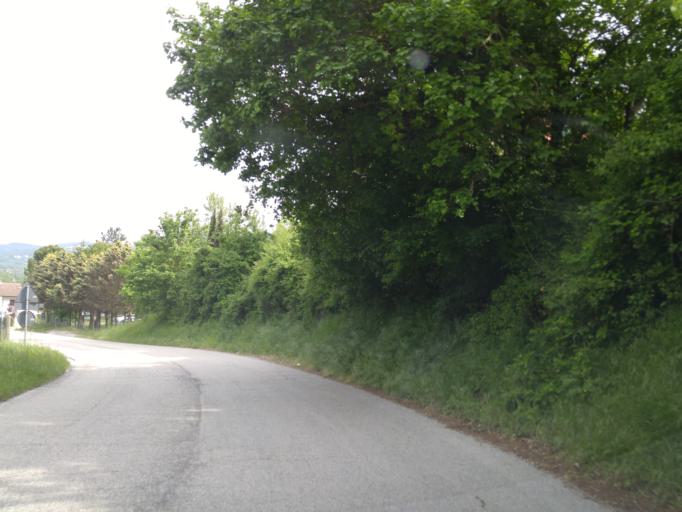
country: IT
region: The Marches
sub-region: Provincia di Pesaro e Urbino
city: Acqualagna
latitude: 43.6287
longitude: 12.6732
